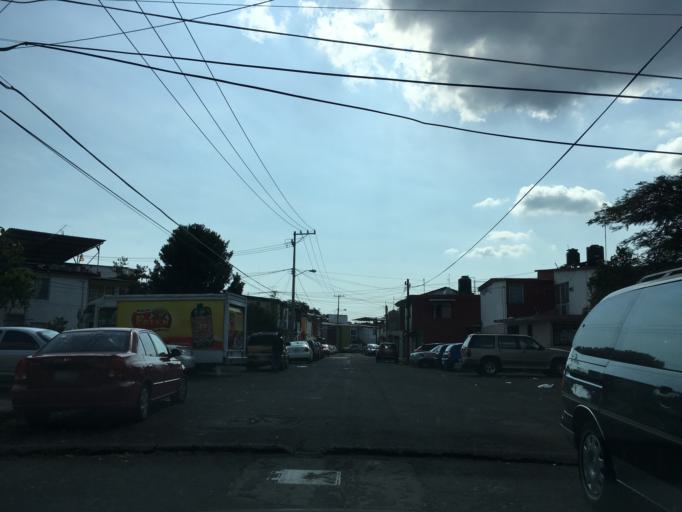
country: MX
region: Michoacan
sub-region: Uruapan
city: Uruapan
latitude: 19.3955
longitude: -102.0511
